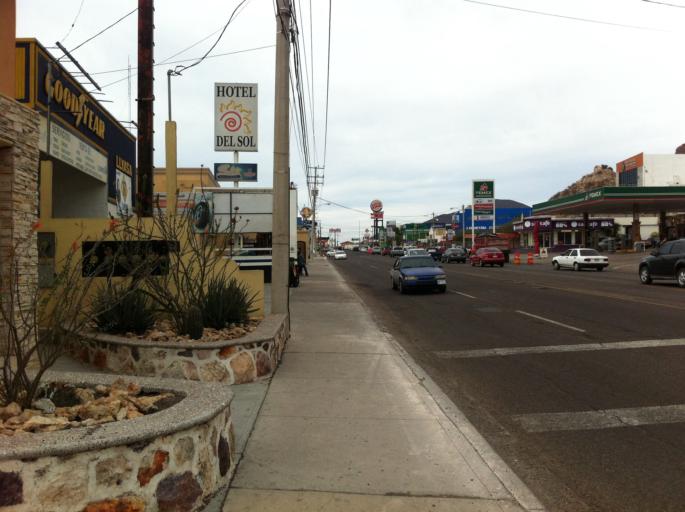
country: MX
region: Sonora
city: Heroica Guaymas
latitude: 27.9255
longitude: -110.9147
